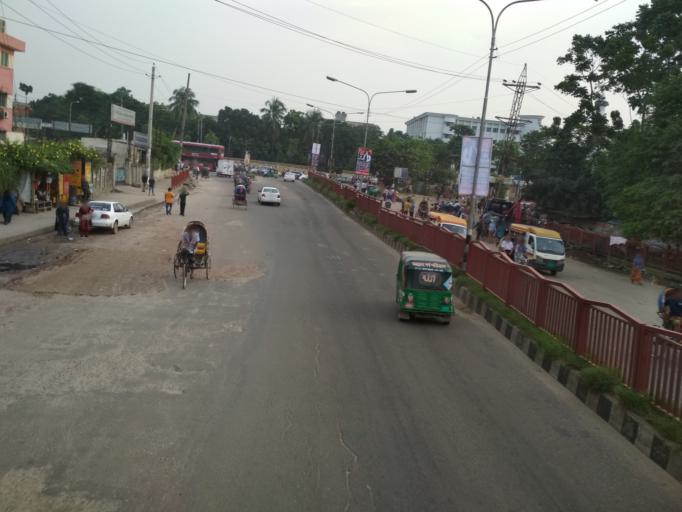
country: BD
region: Dhaka
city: Azimpur
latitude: 23.7825
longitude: 90.3524
